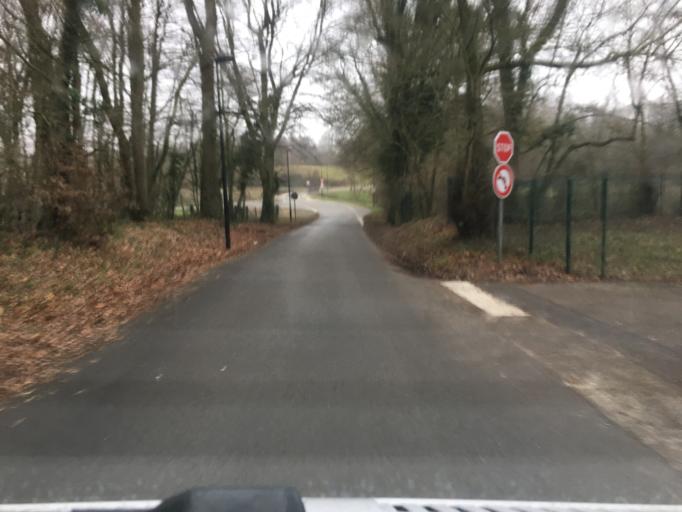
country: FR
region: Picardie
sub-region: Departement de la Somme
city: Saint-Valery-sur-Somme
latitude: 50.1772
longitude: 1.6365
